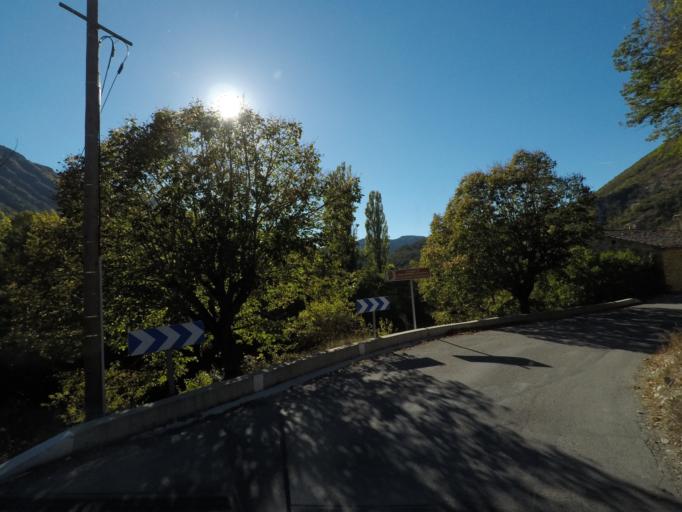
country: FR
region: Rhone-Alpes
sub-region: Departement de la Drome
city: Buis-les-Baronnies
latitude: 44.4697
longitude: 5.4505
